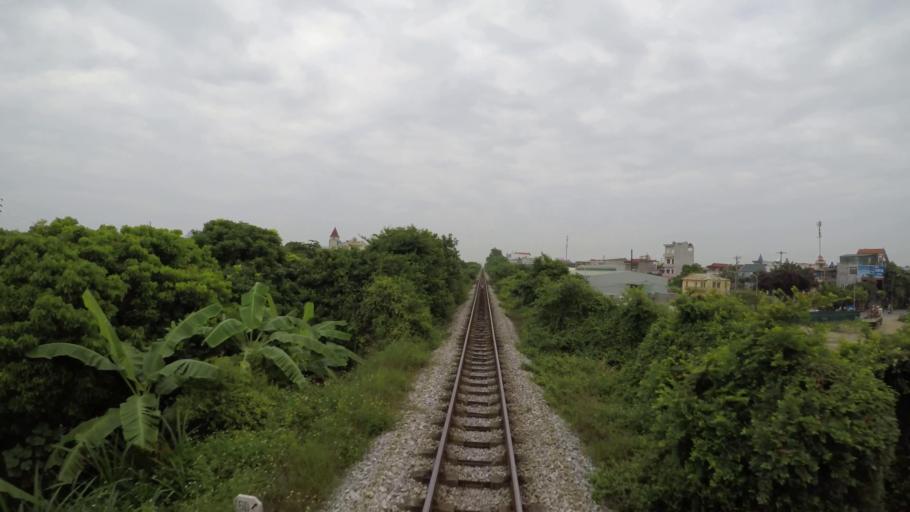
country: VN
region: Hai Duong
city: Thanh Pho Hai Duong
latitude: 20.9491
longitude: 106.3618
